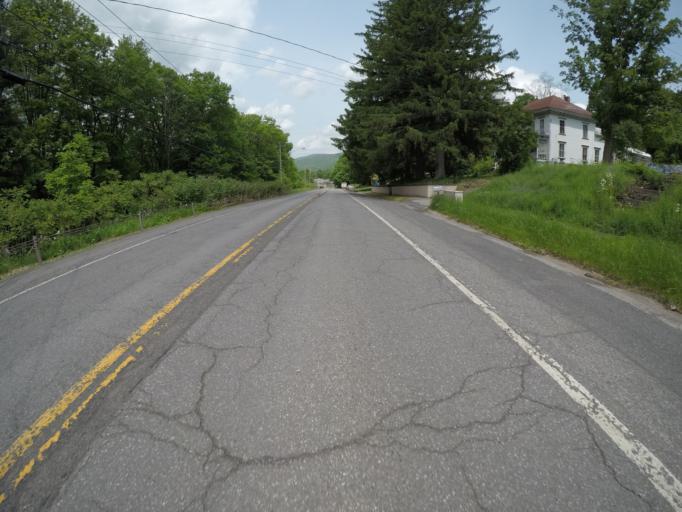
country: US
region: New York
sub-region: Delaware County
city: Stamford
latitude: 42.2812
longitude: -74.5667
